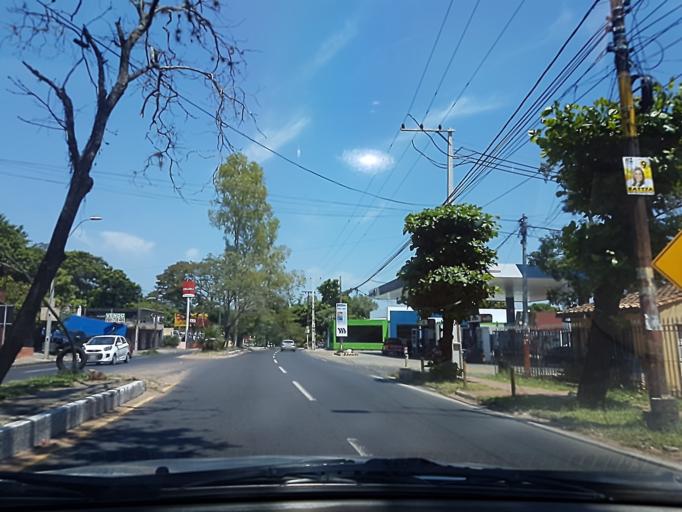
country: PY
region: Central
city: Fernando de la Mora
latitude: -25.3071
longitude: -57.5473
